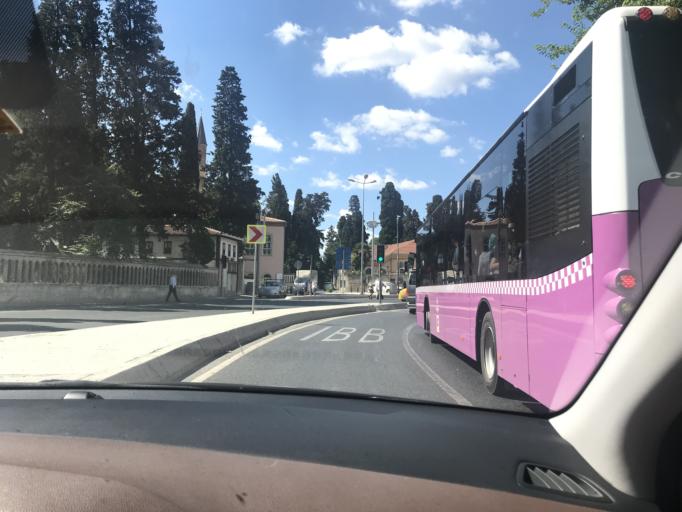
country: TR
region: Istanbul
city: UEskuedar
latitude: 41.0125
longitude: 29.0202
